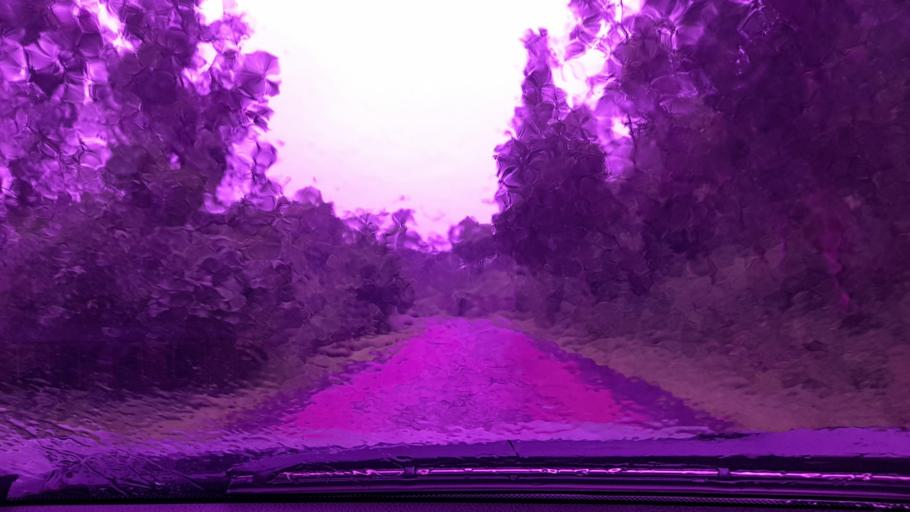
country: ET
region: Oromiya
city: Metu
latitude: 8.4711
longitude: 35.6383
